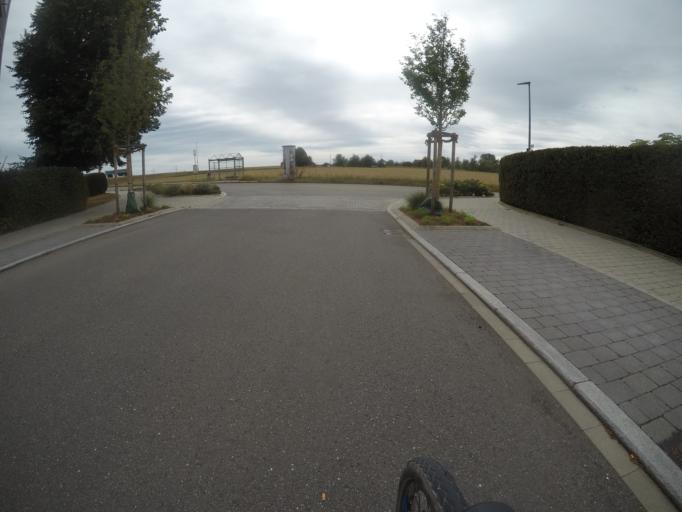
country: DE
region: Baden-Wuerttemberg
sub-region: Regierungsbezirk Stuttgart
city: Vaihingen an der Enz
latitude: 48.9506
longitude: 8.9774
